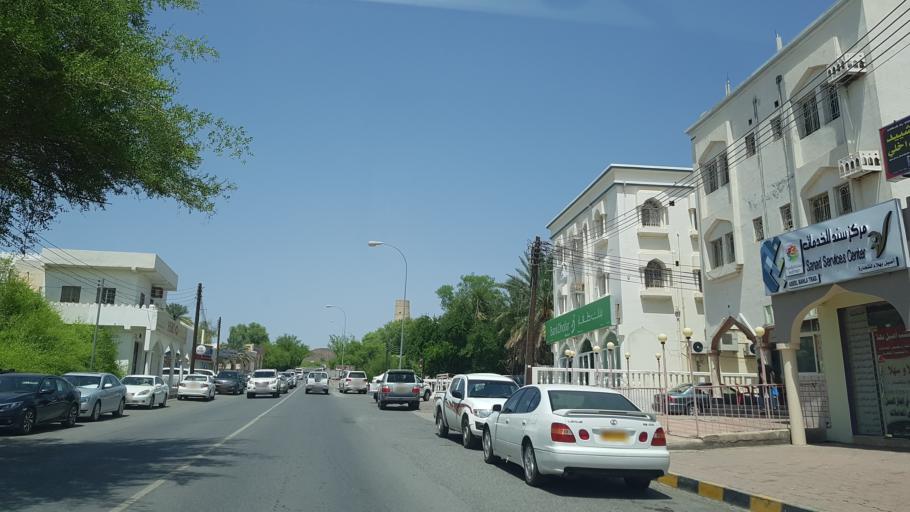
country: OM
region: Muhafazat ad Dakhiliyah
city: Bahla'
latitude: 22.9625
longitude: 57.2987
